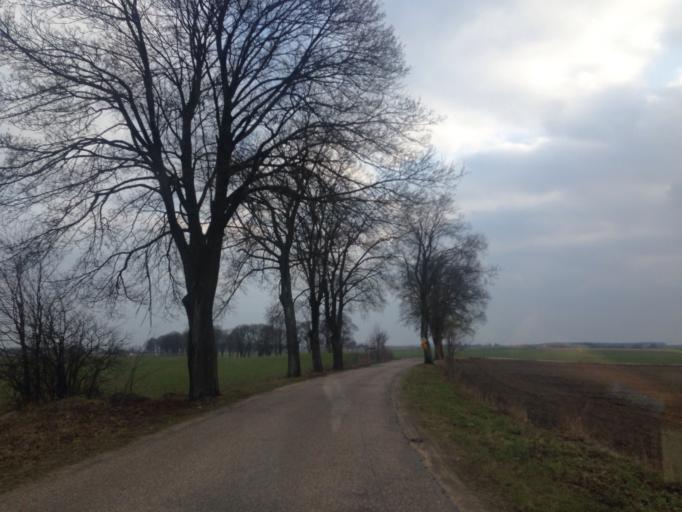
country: PL
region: Kujawsko-Pomorskie
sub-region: Powiat brodnicki
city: Brzozie
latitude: 53.3510
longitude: 19.7070
